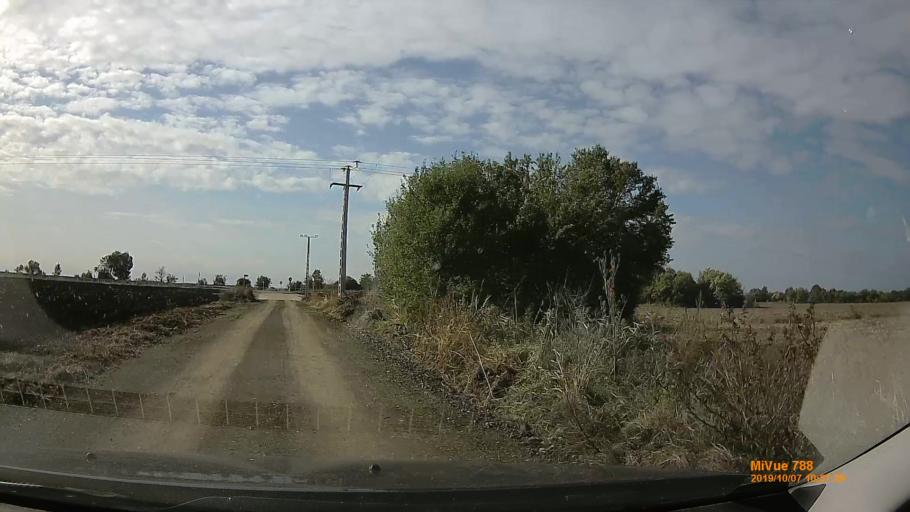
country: HU
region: Bekes
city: Kondoros
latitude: 46.7494
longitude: 20.8484
